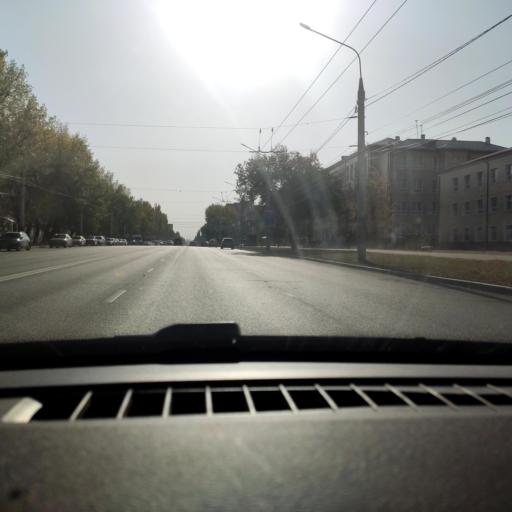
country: RU
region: Voronezj
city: Voronezh
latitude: 51.6573
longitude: 39.2448
